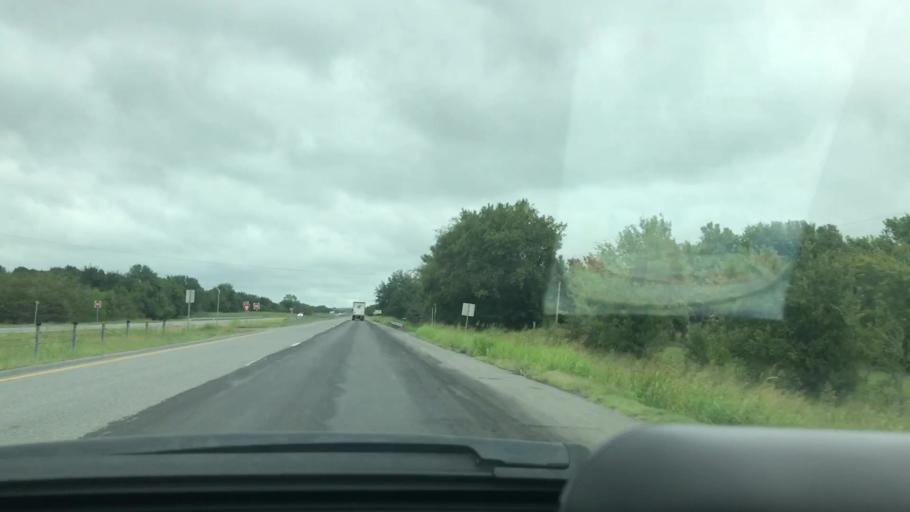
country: US
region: Oklahoma
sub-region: Pittsburg County
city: McAlester
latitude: 34.7993
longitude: -95.8689
